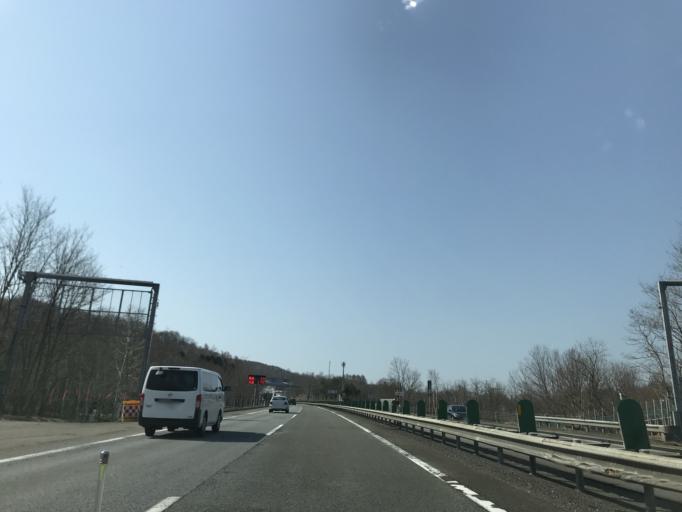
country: JP
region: Hokkaido
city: Bibai
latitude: 43.3159
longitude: 141.8833
